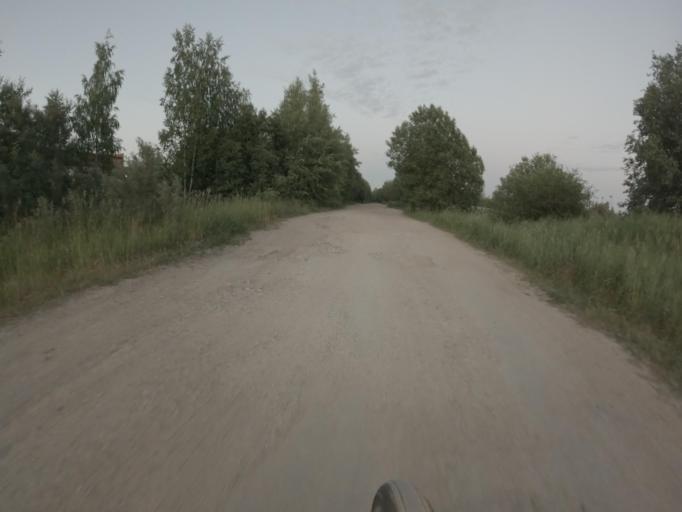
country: RU
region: St.-Petersburg
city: Sapernyy
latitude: 59.7806
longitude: 30.6644
